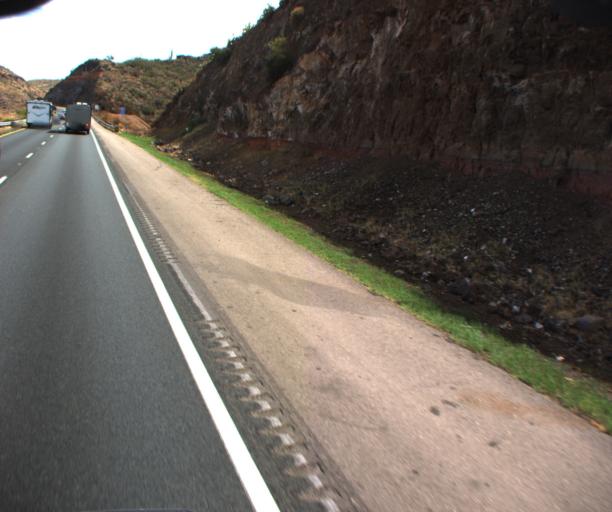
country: US
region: Arizona
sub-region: Yavapai County
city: Black Canyon City
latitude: 34.1422
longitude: -112.1430
